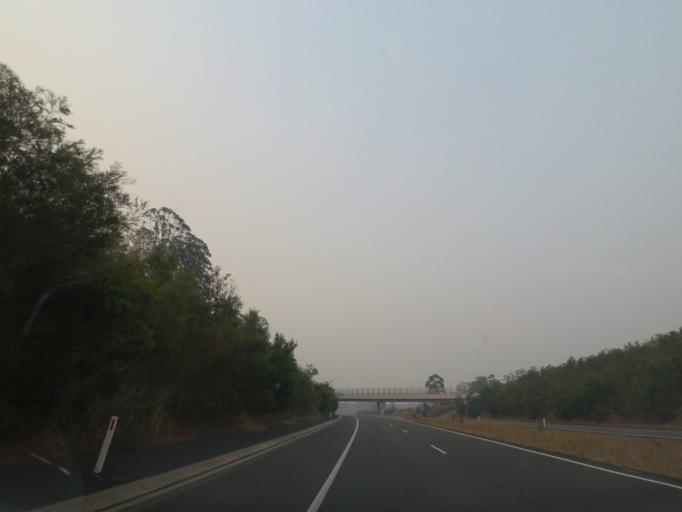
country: AU
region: New South Wales
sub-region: Nambucca Shire
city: Macksville
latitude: -30.7654
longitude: 152.9037
